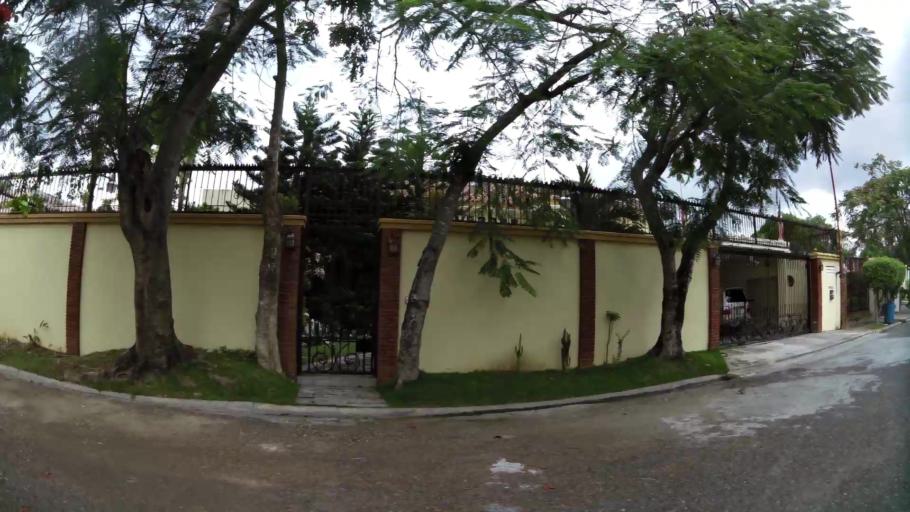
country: DO
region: Nacional
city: La Agustina
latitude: 18.5037
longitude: -69.9342
